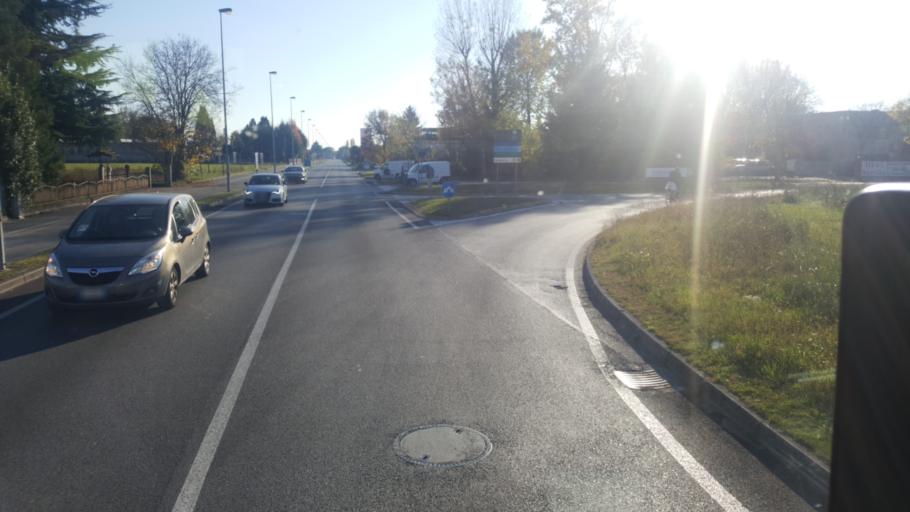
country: IT
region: Friuli Venezia Giulia
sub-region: Provincia di Pordenone
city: Pordenone
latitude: 45.9328
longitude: 12.6581
